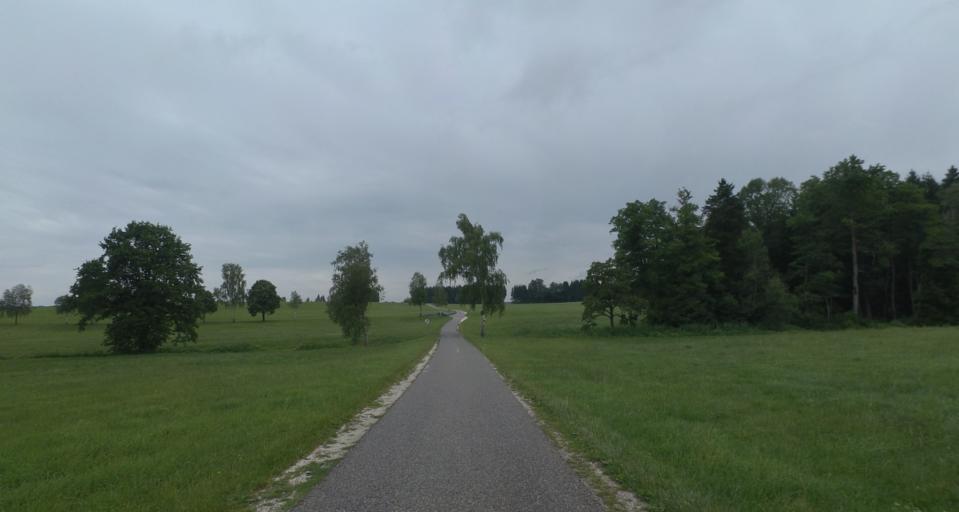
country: DE
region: Bavaria
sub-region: Upper Bavaria
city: Grabenstatt
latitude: 47.8245
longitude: 12.5273
